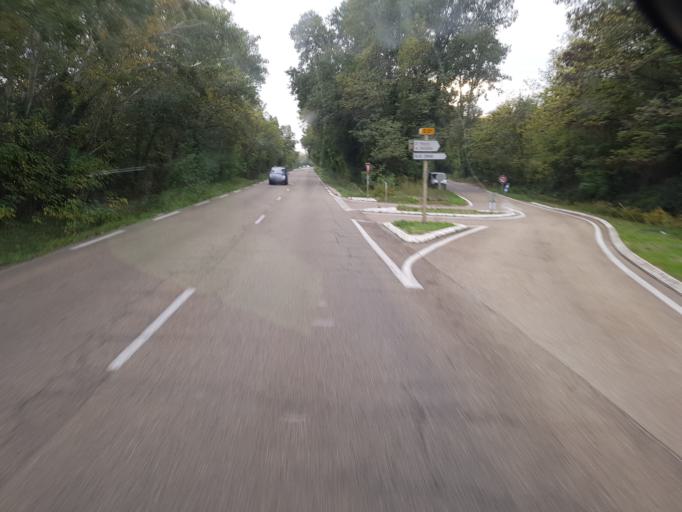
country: FR
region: Provence-Alpes-Cote d'Azur
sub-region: Departement des Bouches-du-Rhone
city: Barbentane
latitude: 43.9264
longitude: 4.7370
